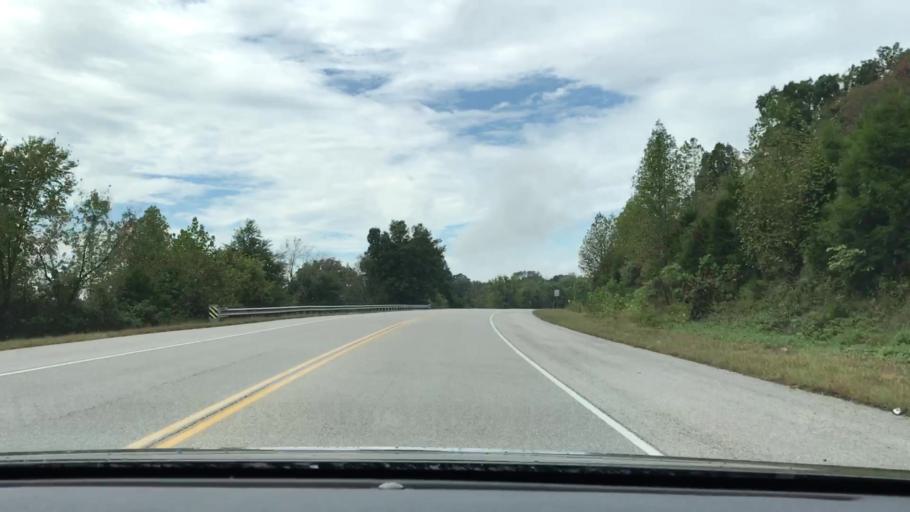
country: US
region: Tennessee
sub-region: Macon County
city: Red Boiling Springs
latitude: 36.5189
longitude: -85.8490
